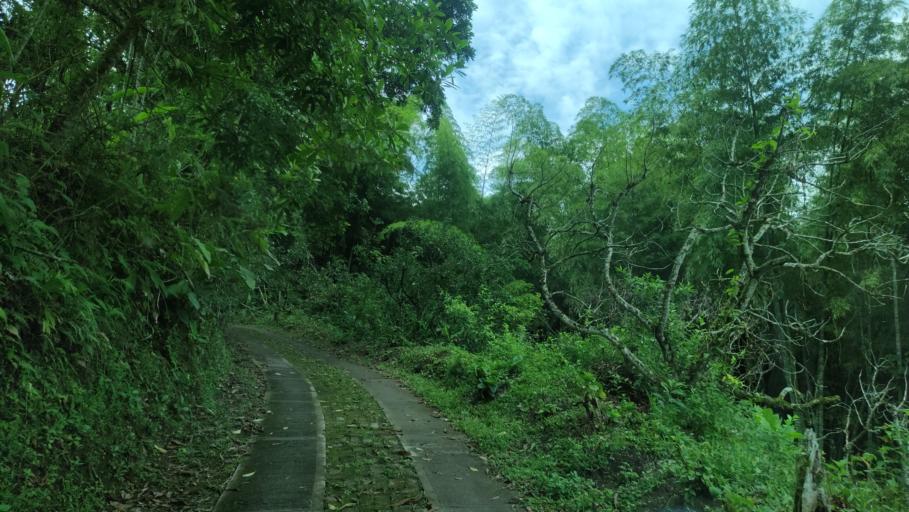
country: CO
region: Caldas
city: Palestina
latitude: 5.0669
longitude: -75.5925
